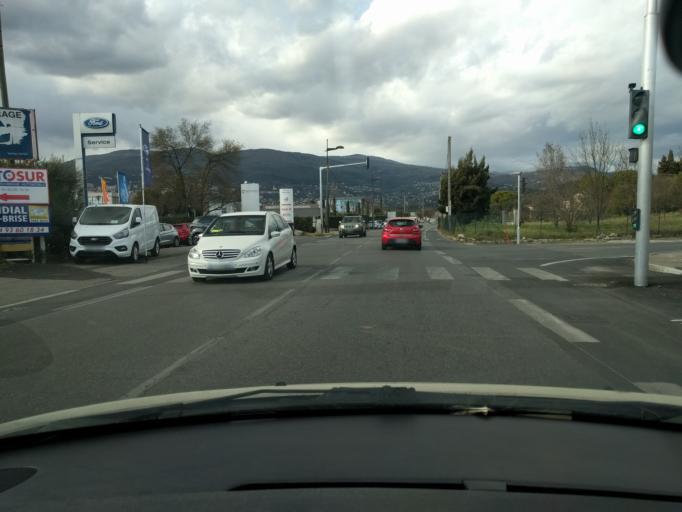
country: FR
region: Provence-Alpes-Cote d'Azur
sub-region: Departement des Alpes-Maritimes
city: Mouans-Sartoux
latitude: 43.6360
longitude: 6.9567
